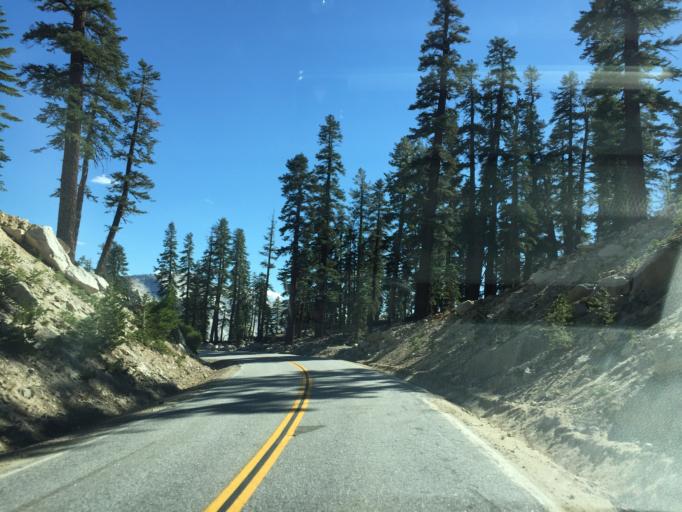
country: US
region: California
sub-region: Mariposa County
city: Yosemite Valley
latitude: 37.8124
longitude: -119.5095
